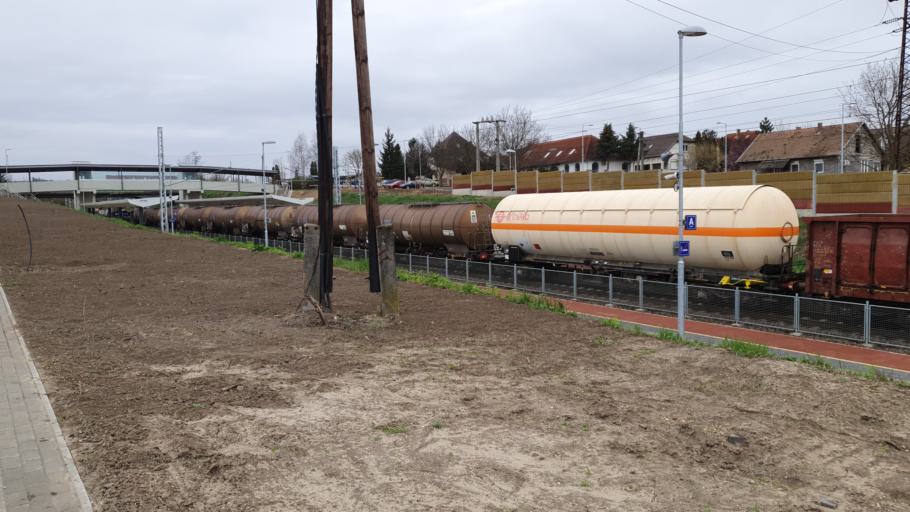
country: HU
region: Pest
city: Aszod
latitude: 47.6408
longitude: 19.4716
